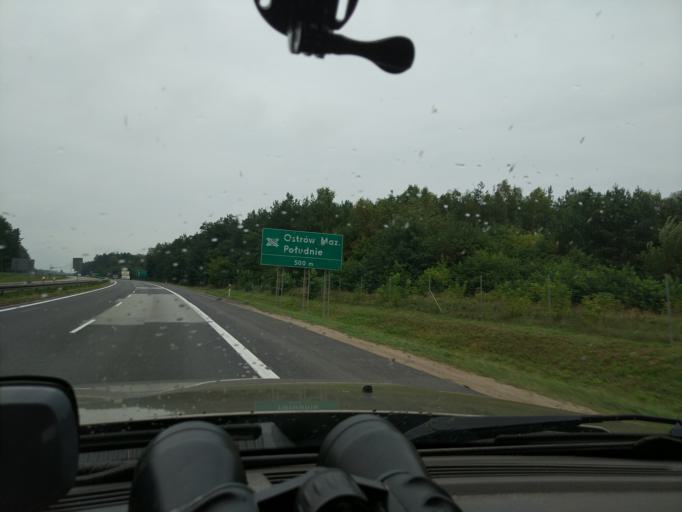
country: PL
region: Masovian Voivodeship
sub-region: Powiat ostrowski
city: Ostrow Mazowiecka
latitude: 52.7895
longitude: 21.8657
